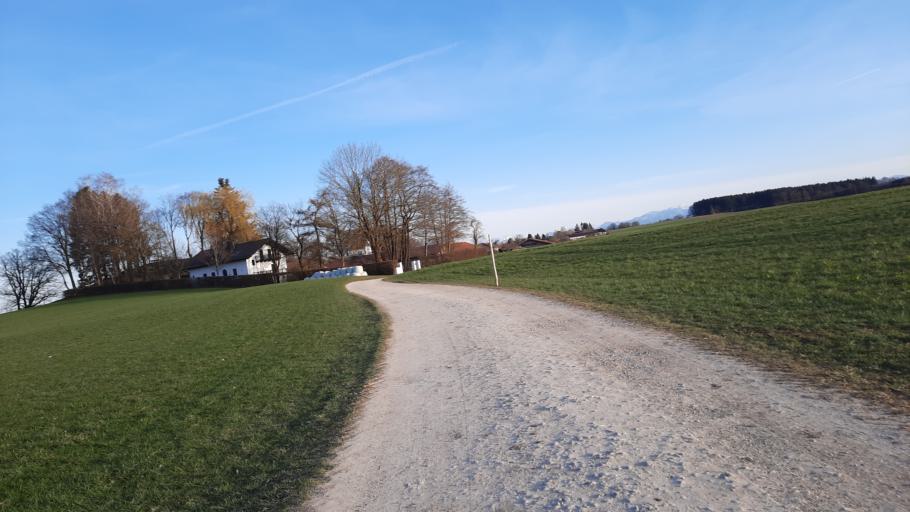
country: DE
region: Bavaria
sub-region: Upper Bavaria
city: Ebersberg
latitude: 48.0830
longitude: 11.9343
